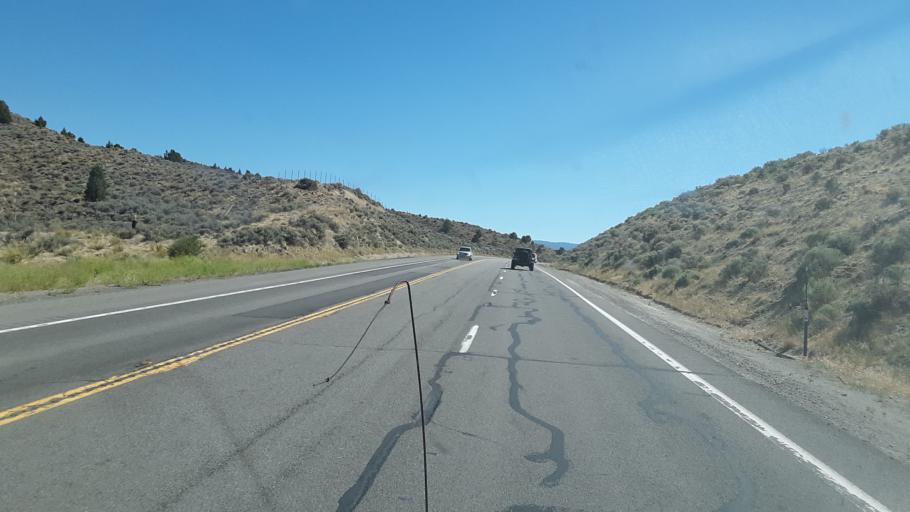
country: US
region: Nevada
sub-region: Washoe County
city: Cold Springs
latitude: 39.8702
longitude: -120.0360
